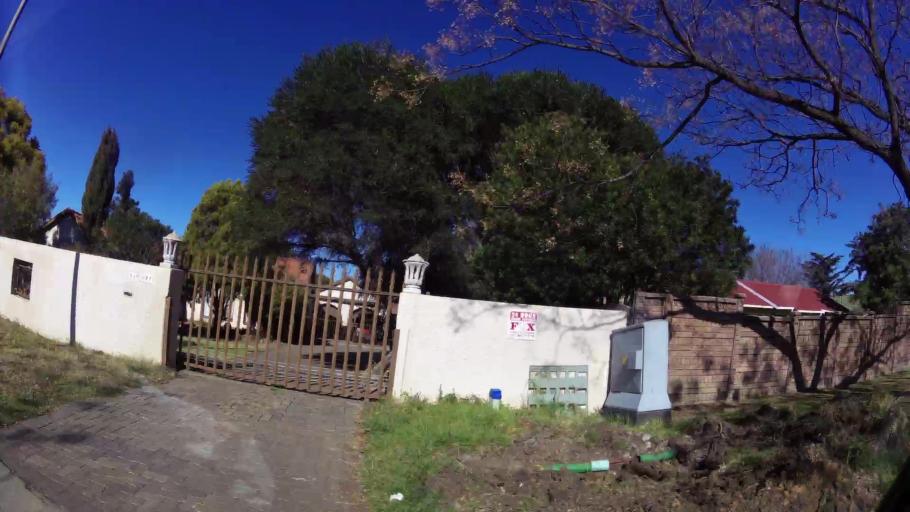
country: ZA
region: Gauteng
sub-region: Ekurhuleni Metropolitan Municipality
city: Germiston
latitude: -26.3311
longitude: 28.1075
